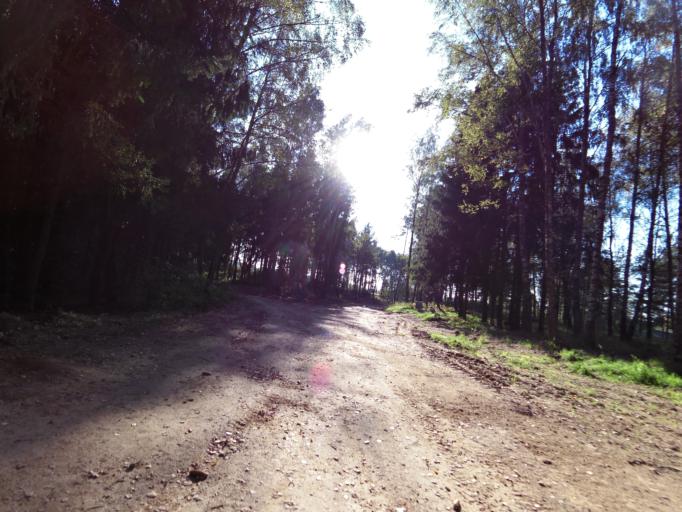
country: LT
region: Vilnius County
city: Pilaite
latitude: 54.7182
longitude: 25.1907
